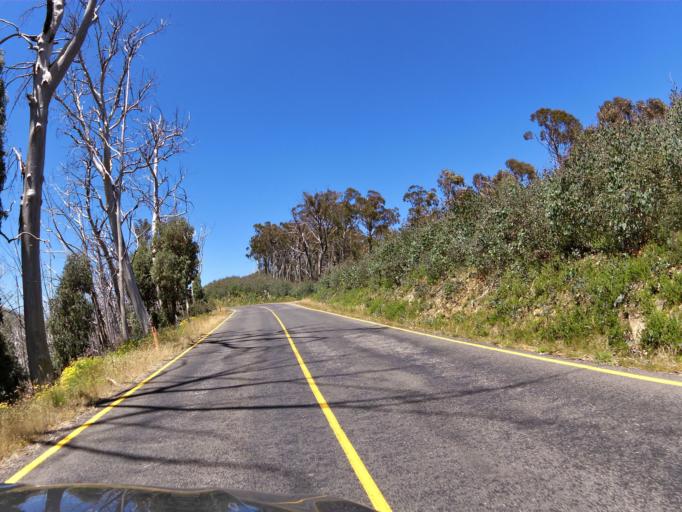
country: AU
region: Victoria
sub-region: Alpine
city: Mount Beauty
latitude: -37.0011
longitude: 147.0716
